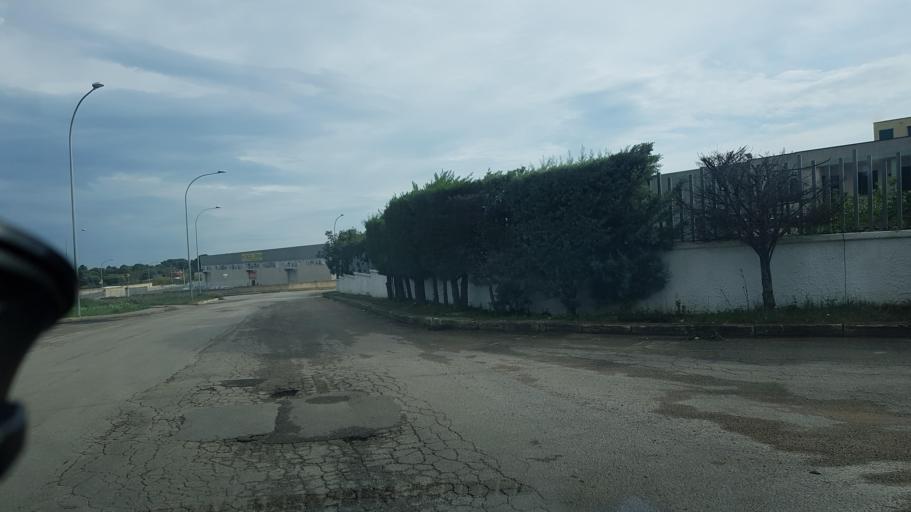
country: IT
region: Apulia
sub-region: Provincia di Brindisi
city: San Vito dei Normanni
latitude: 40.6660
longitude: 17.7014
